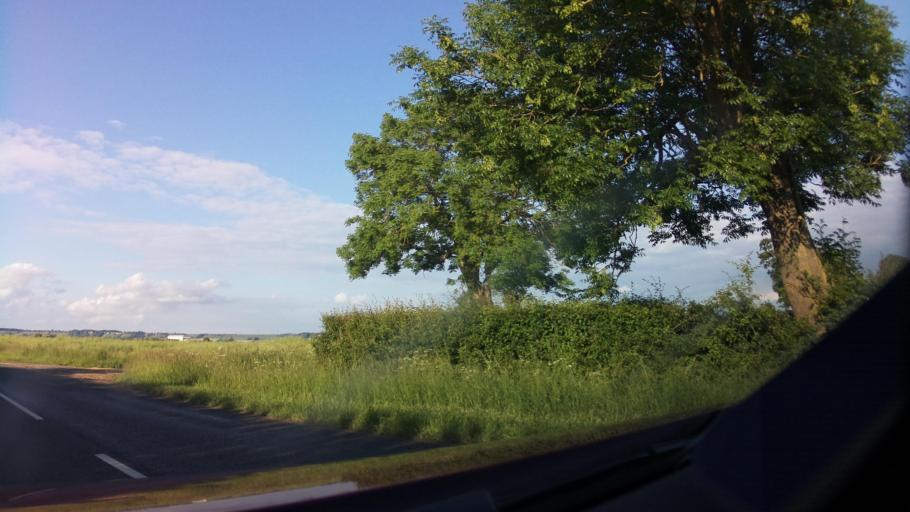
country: GB
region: England
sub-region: Lincolnshire
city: Navenby
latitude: 53.1025
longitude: -0.6087
